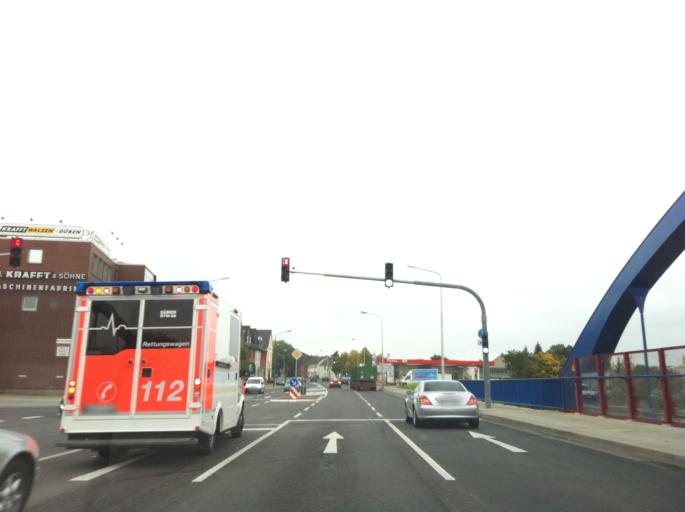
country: DE
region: North Rhine-Westphalia
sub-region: Regierungsbezirk Koln
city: Dueren
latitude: 50.8149
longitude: 6.4881
